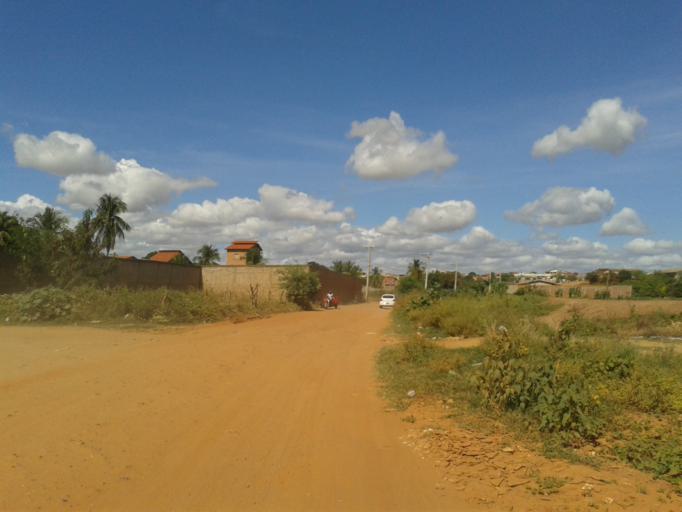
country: BR
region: Bahia
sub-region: Livramento Do Brumado
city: Livramento do Brumado
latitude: -13.6530
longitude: -41.8449
